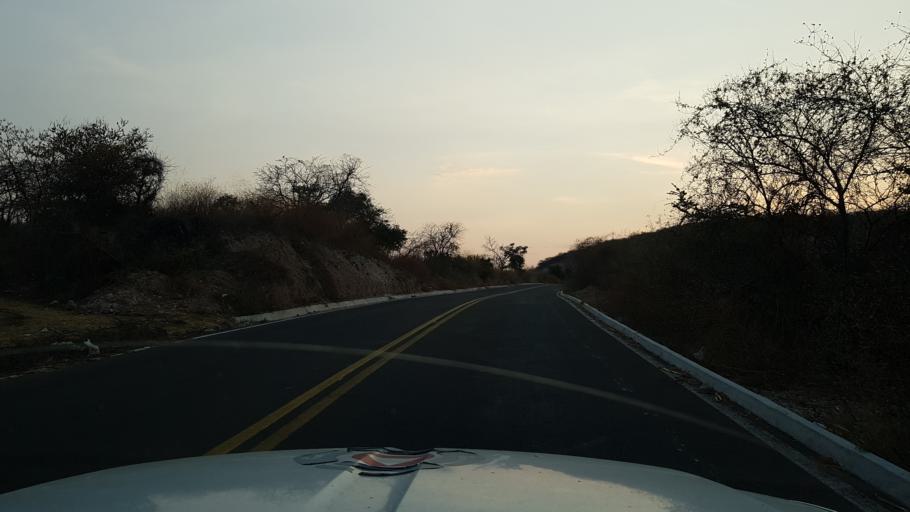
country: MX
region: Morelos
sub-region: Ayala
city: Olintepec
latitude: 18.7332
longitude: -99.0156
